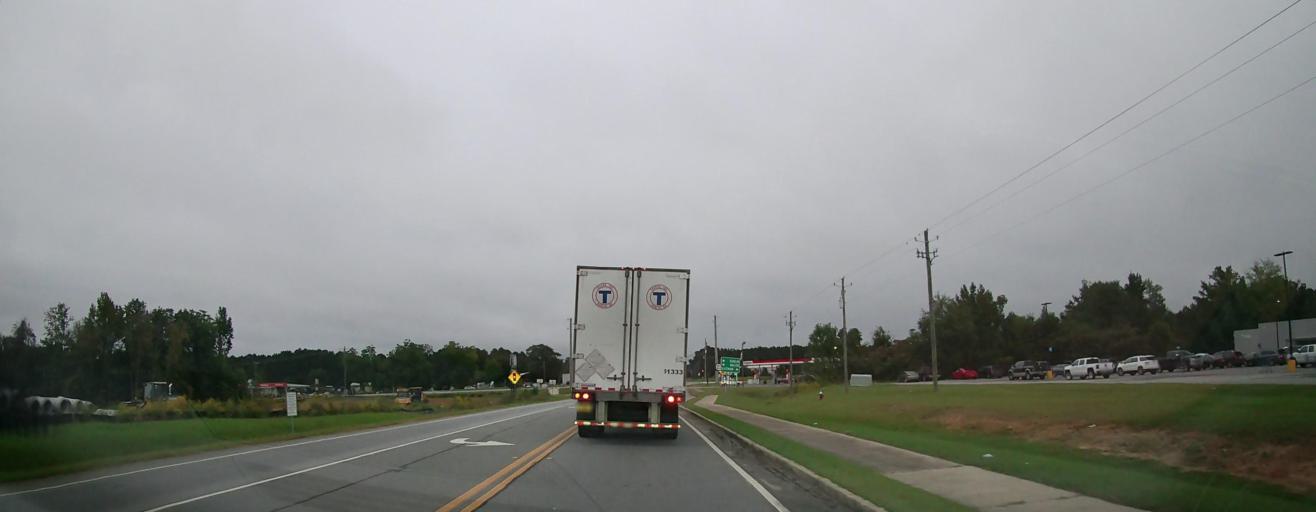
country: US
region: Georgia
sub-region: Bleckley County
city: Cochran
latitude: 32.4009
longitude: -83.3378
